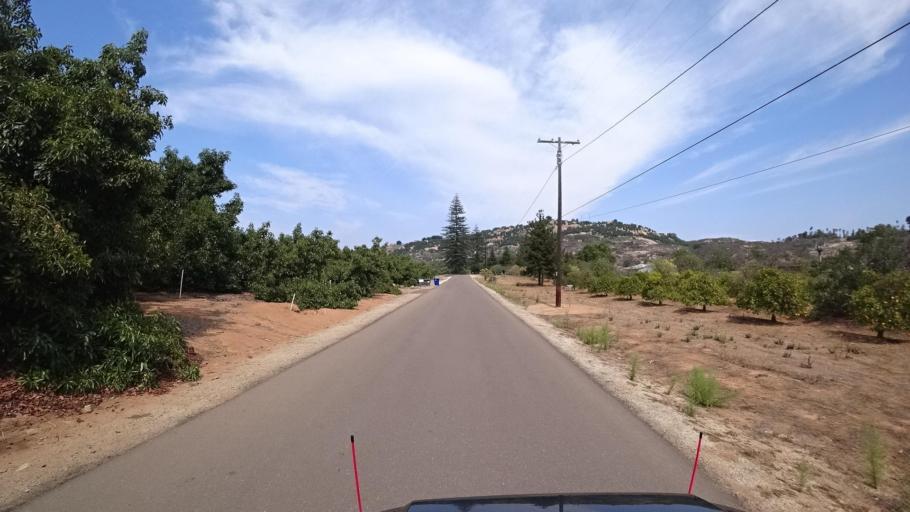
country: US
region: California
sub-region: San Diego County
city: Escondido
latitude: 33.1140
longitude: -117.0348
